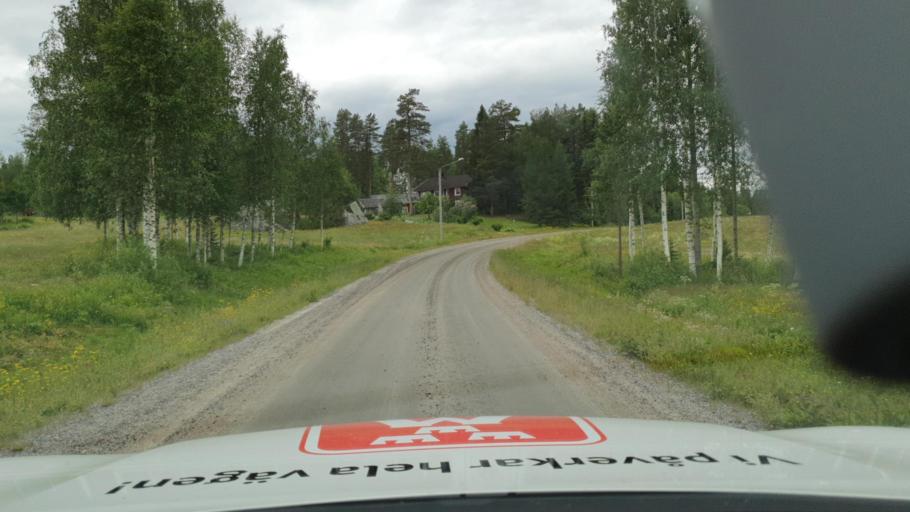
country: SE
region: Vaesterbotten
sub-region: Bjurholms Kommun
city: Bjurholm
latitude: 63.7425
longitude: 19.2794
